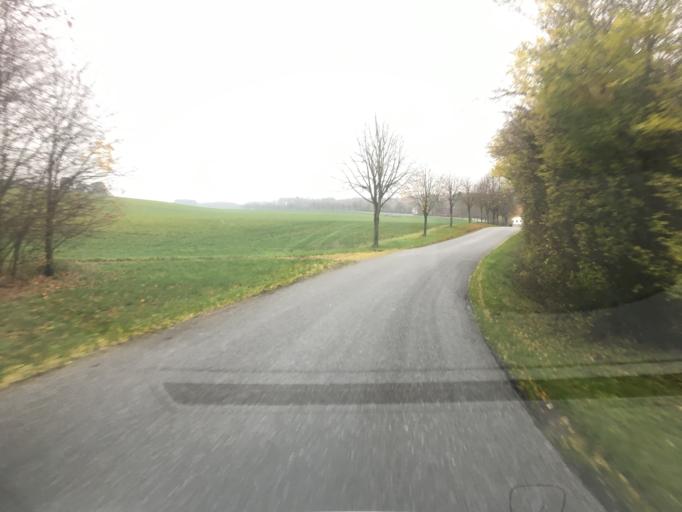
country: DK
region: Central Jutland
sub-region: Randers Kommune
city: Assentoft
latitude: 56.3976
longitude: 10.1850
